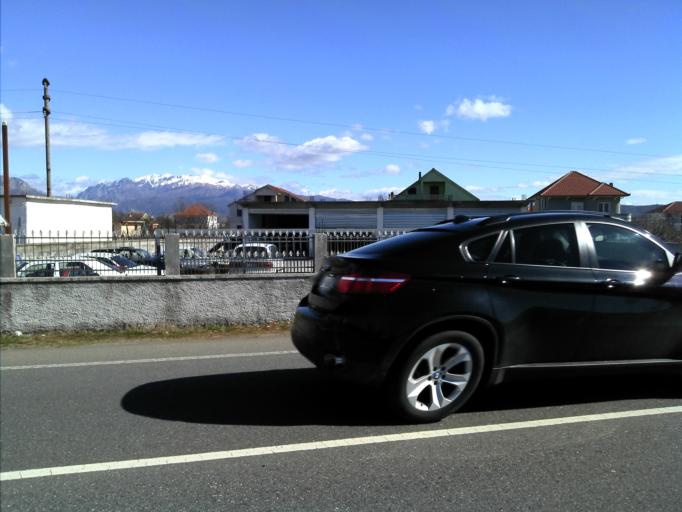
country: AL
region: Shkoder
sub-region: Rrethi i Shkodres
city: Shkoder
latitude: 42.1006
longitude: 19.5050
